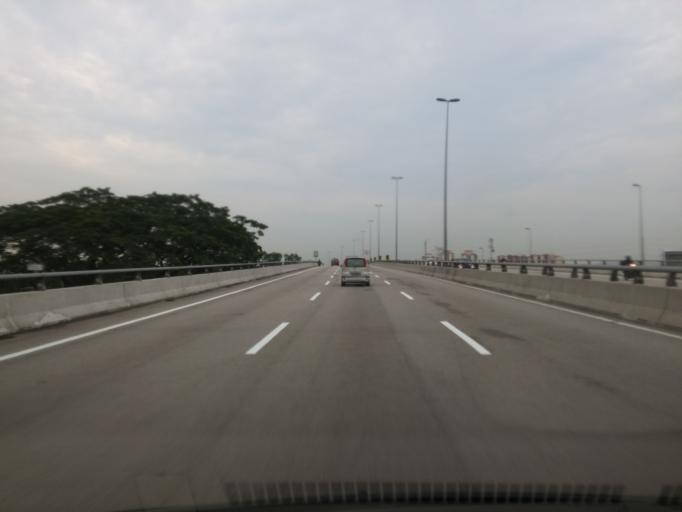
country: MY
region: Kuala Lumpur
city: Kuala Lumpur
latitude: 3.0988
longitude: 101.7001
